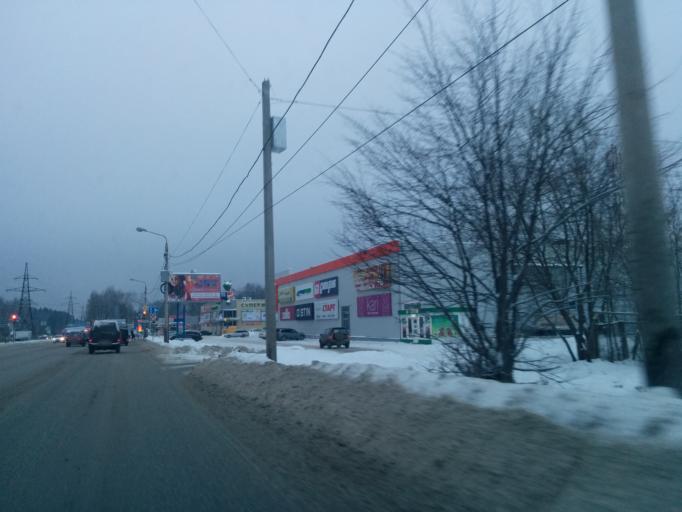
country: RU
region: Perm
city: Kondratovo
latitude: 58.0391
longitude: 56.0286
